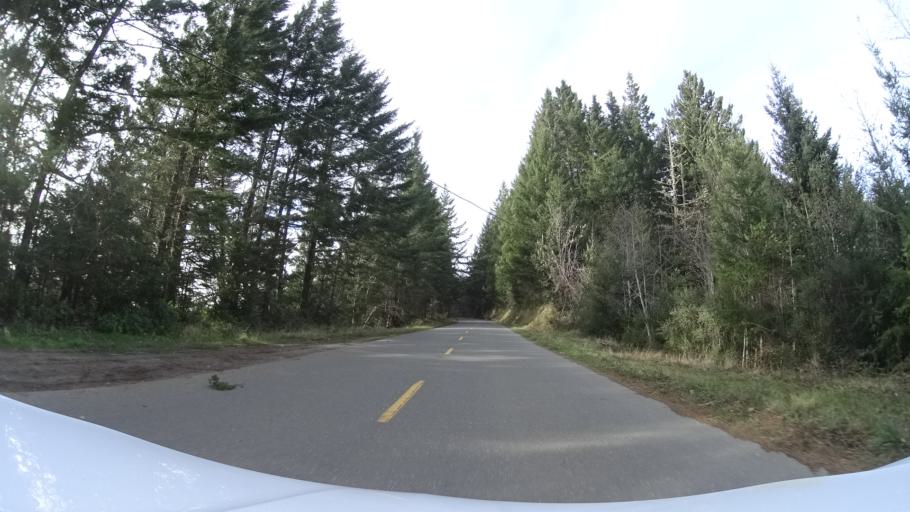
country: US
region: California
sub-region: Humboldt County
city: Ferndale
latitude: 40.5341
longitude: -124.2699
